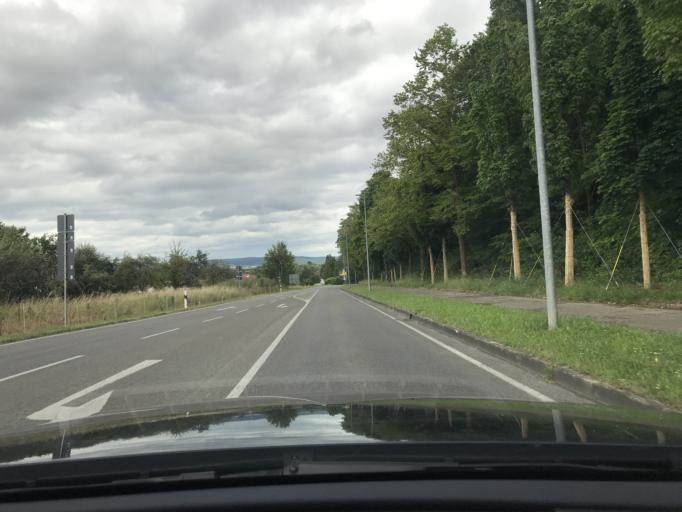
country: DE
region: Baden-Wuerttemberg
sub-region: Regierungsbezirk Stuttgart
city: Stuttgart Muehlhausen
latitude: 48.8328
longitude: 9.2537
